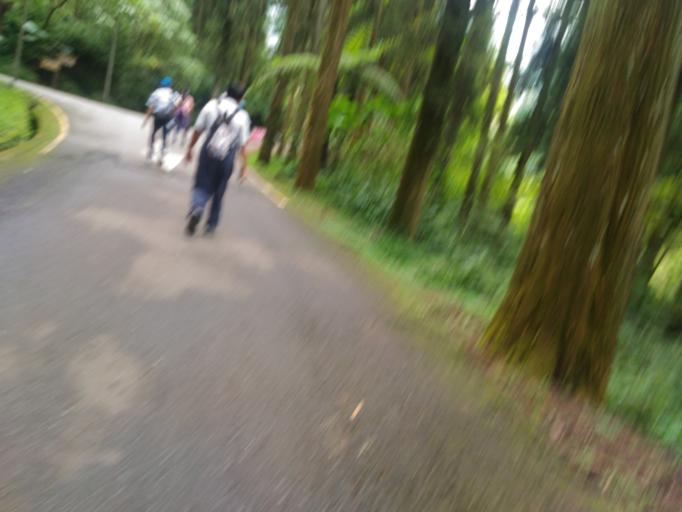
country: TW
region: Taiwan
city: Lugu
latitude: 23.6687
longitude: 120.7983
